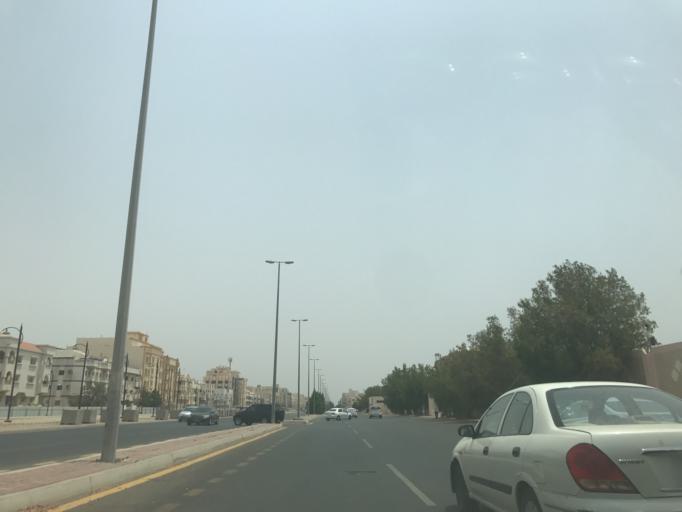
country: SA
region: Makkah
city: Jeddah
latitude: 21.5922
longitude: 39.1462
